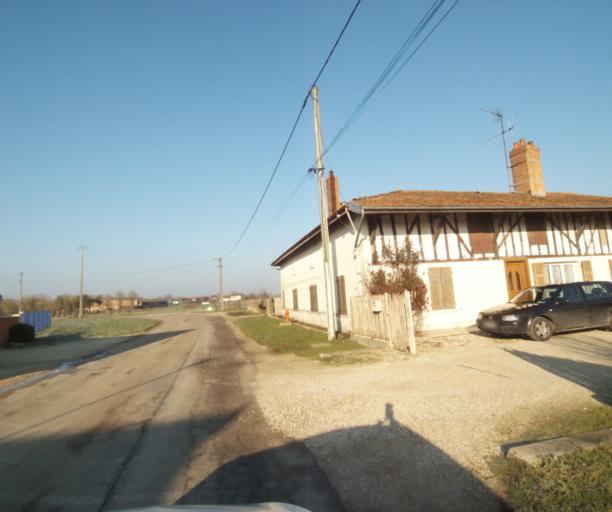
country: FR
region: Champagne-Ardenne
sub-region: Departement de la Haute-Marne
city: Montier-en-Der
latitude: 48.4785
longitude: 4.7567
